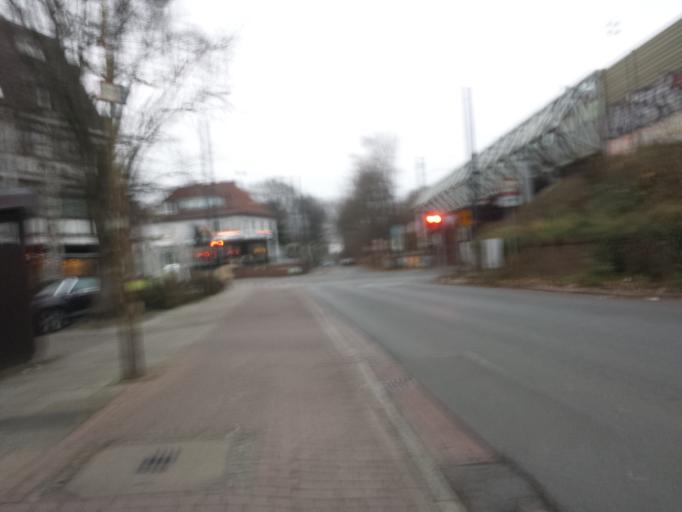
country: DE
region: Lower Saxony
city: Lilienthal
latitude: 53.0986
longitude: 8.8702
